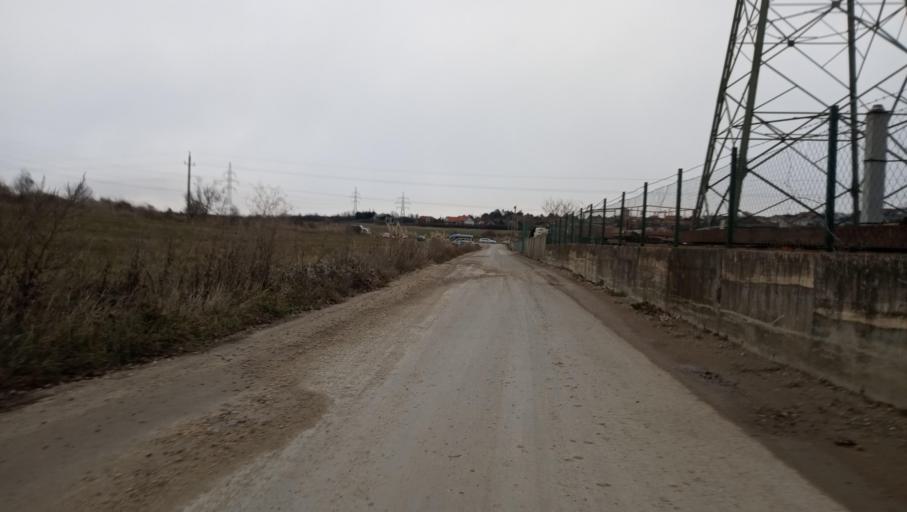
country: HU
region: Pest
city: Urom
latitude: 47.5992
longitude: 19.0224
